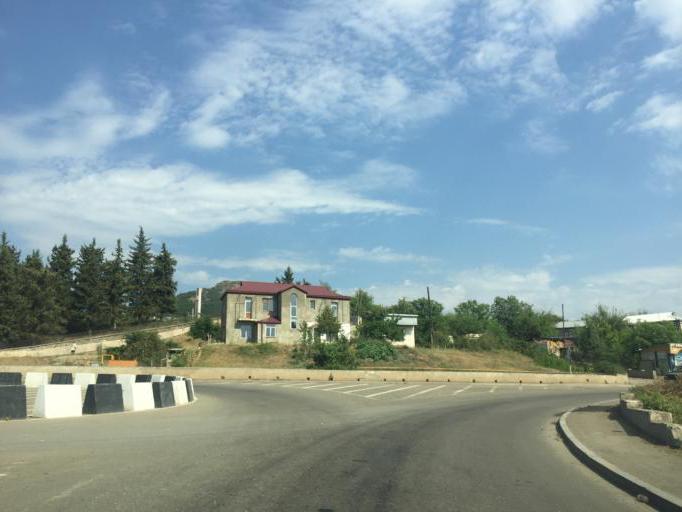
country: AZ
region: Xankandi Sahari
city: Xankandi
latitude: 39.8722
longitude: 46.7306
